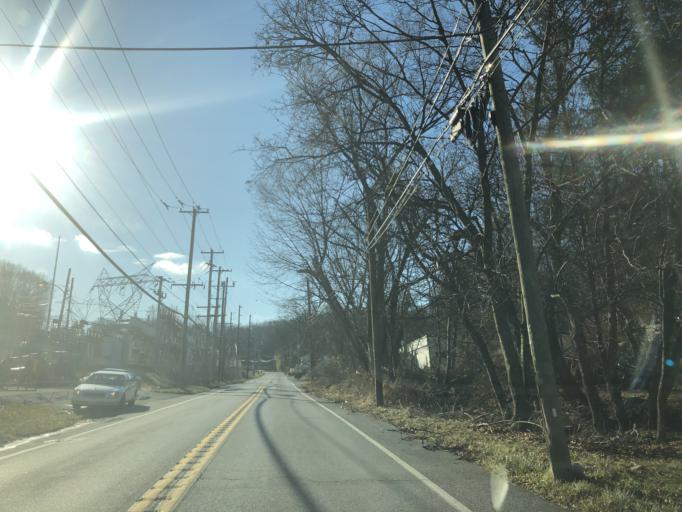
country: US
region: Pennsylvania
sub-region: Chester County
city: South Coatesville
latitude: 39.9729
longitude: -75.8290
